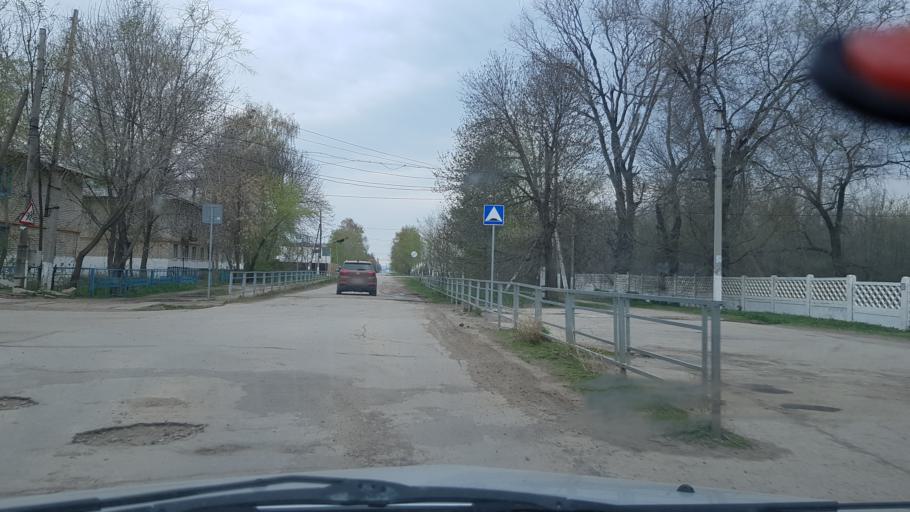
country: RU
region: Samara
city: Khryashchevka
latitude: 53.6722
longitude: 49.0705
